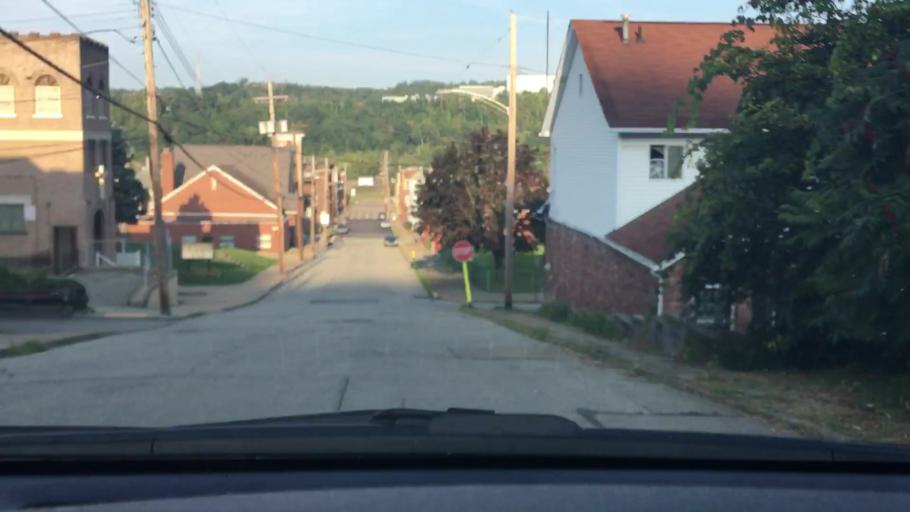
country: US
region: Pennsylvania
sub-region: Allegheny County
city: Glassport
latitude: 40.3277
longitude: -79.8899
